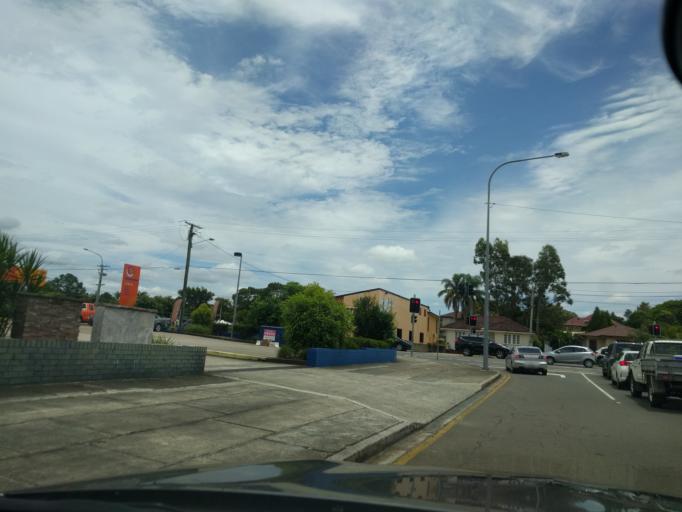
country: AU
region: Queensland
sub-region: Brisbane
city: Stafford
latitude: -27.4101
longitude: 153.0112
